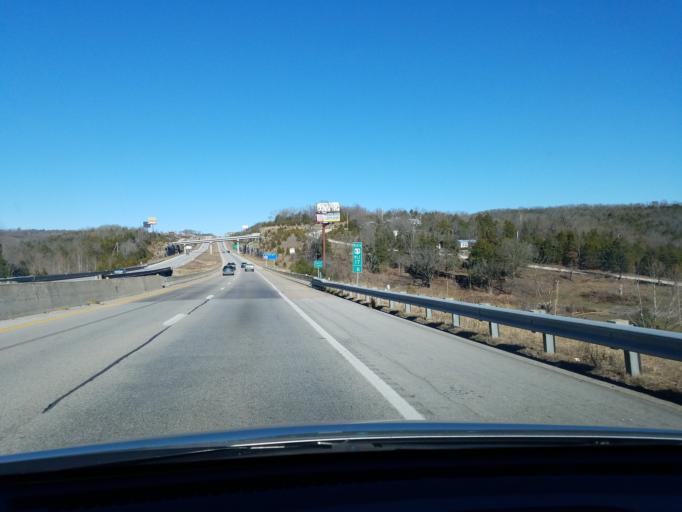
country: US
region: Missouri
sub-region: Taney County
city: Merriam Woods
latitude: 36.7323
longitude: -93.2206
